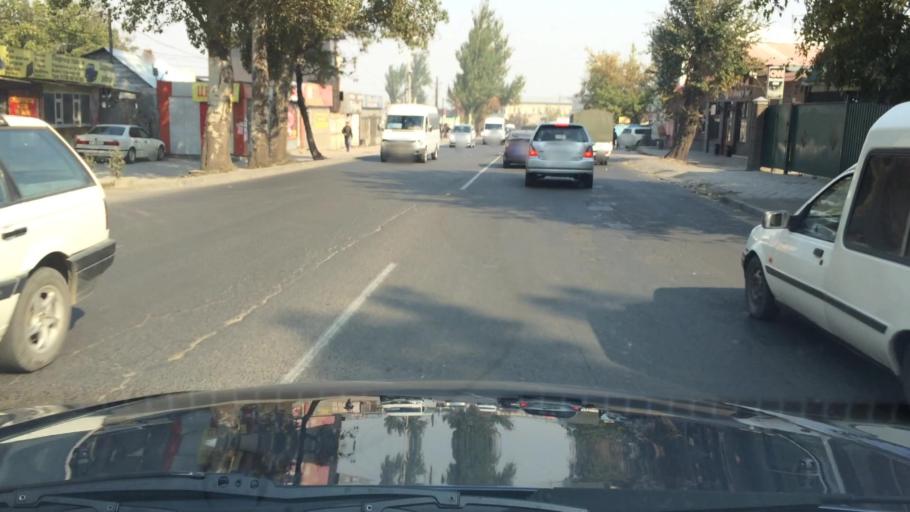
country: KG
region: Chuy
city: Lebedinovka
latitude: 42.8763
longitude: 74.6371
